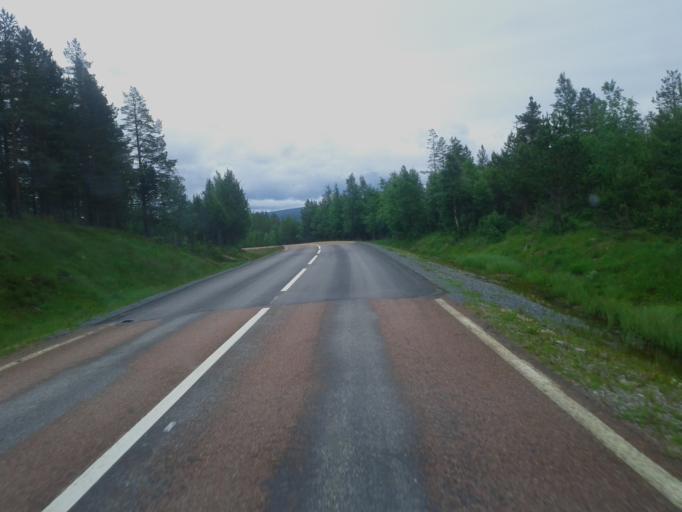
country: NO
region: Hedmark
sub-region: Engerdal
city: Engerdal
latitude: 61.8042
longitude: 12.3984
